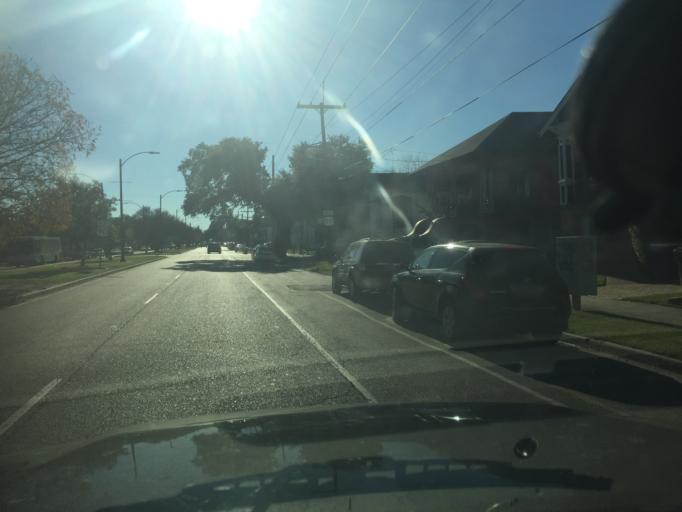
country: US
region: Louisiana
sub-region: Orleans Parish
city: New Orleans
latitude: 29.9831
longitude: -90.0721
